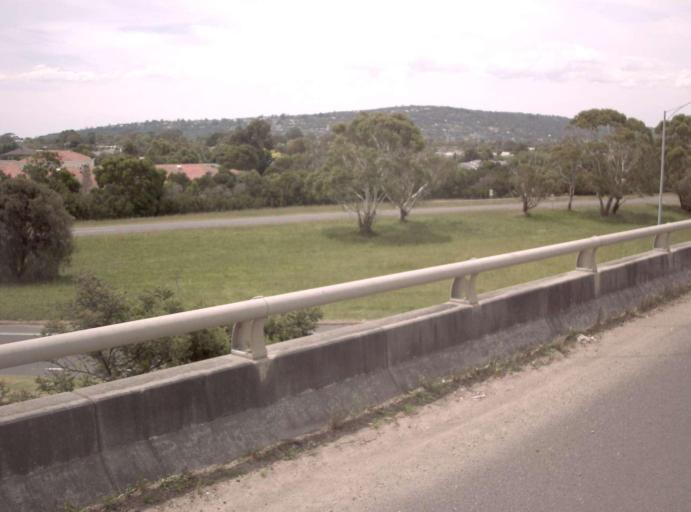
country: AU
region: Victoria
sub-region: Mornington Peninsula
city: Safety Beach
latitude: -38.3301
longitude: 144.9885
